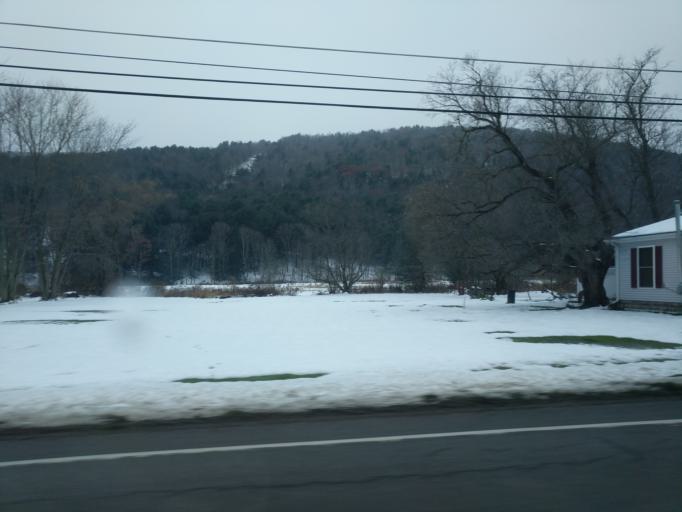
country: US
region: Pennsylvania
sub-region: Tioga County
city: Wellsboro
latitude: 41.8166
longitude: -77.2887
